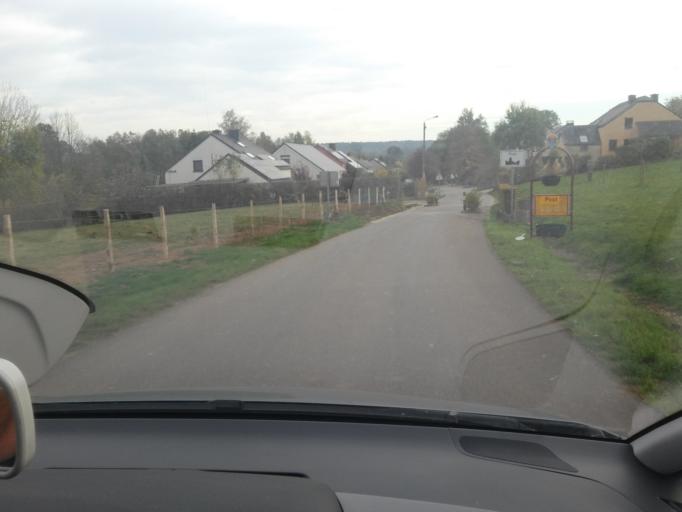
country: BE
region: Wallonia
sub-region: Province du Luxembourg
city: Attert
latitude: 49.7549
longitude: 5.7688
